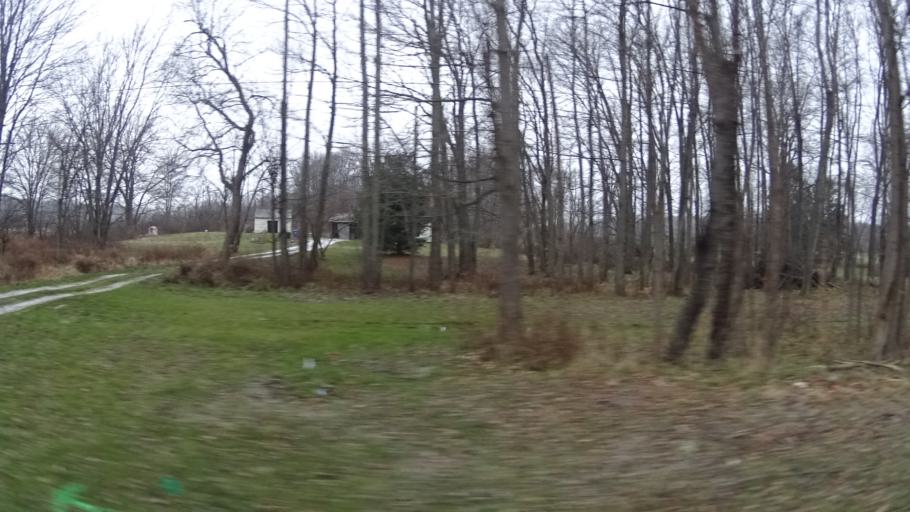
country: US
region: Ohio
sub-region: Lorain County
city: Oberlin
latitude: 41.3053
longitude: -82.2581
